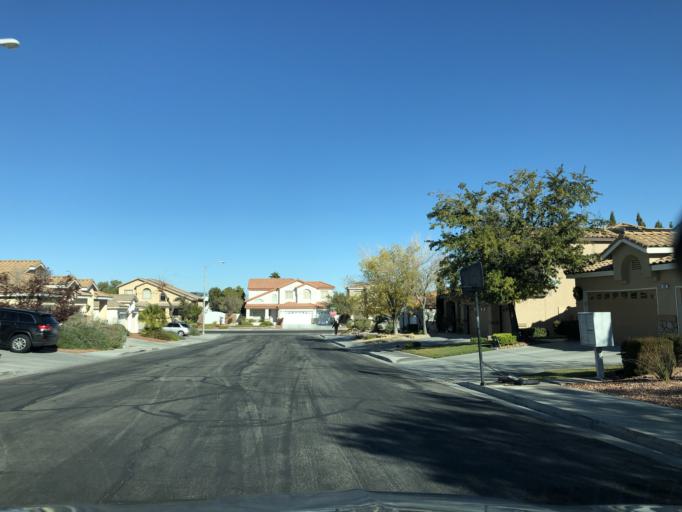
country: US
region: Nevada
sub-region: Clark County
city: Whitney
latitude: 36.0102
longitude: -115.0853
